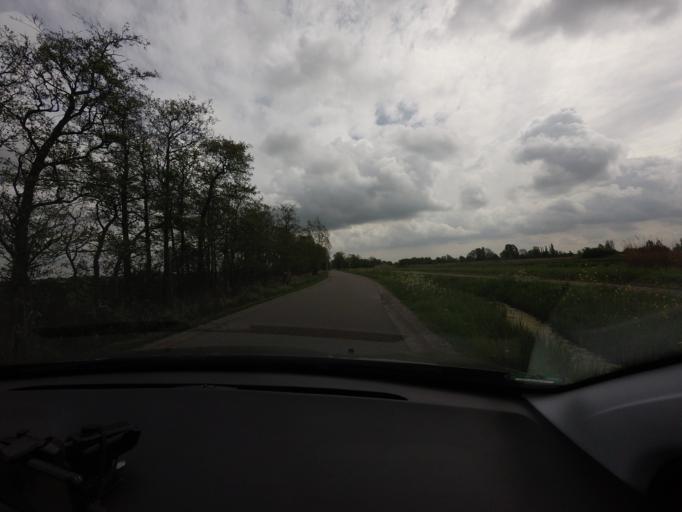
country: NL
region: North Holland
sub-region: Gemeente Landsmeer
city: Landsmeer
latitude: 52.4717
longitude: 4.9066
